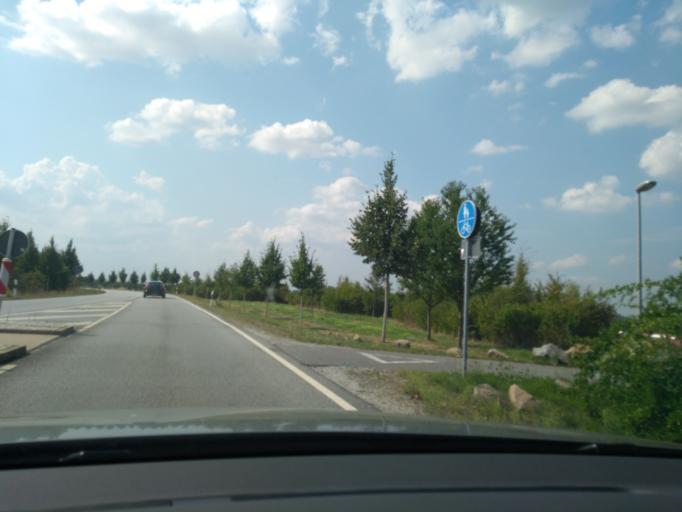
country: DE
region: Saxony
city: Bautzen
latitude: 51.1814
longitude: 14.4091
